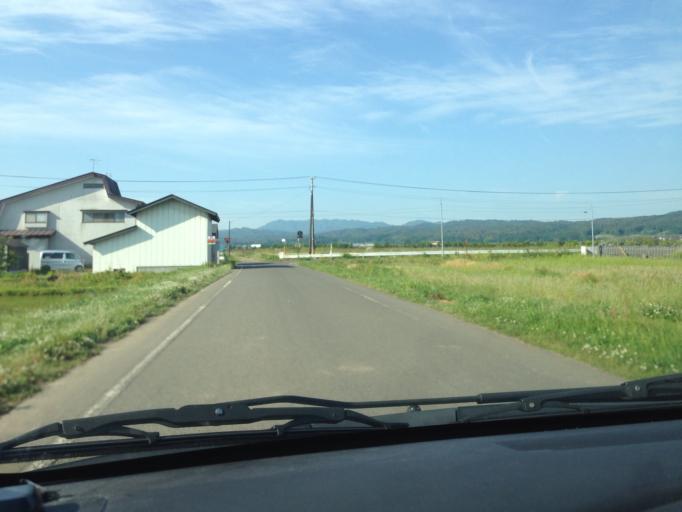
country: JP
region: Fukushima
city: Kitakata
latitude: 37.5438
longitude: 139.8141
